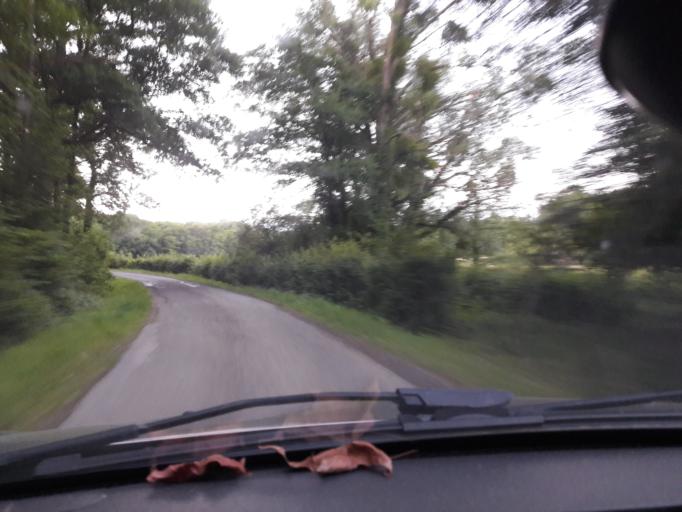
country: BE
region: Wallonia
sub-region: Province du Hainaut
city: Beaumont
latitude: 50.2701
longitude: 4.1949
